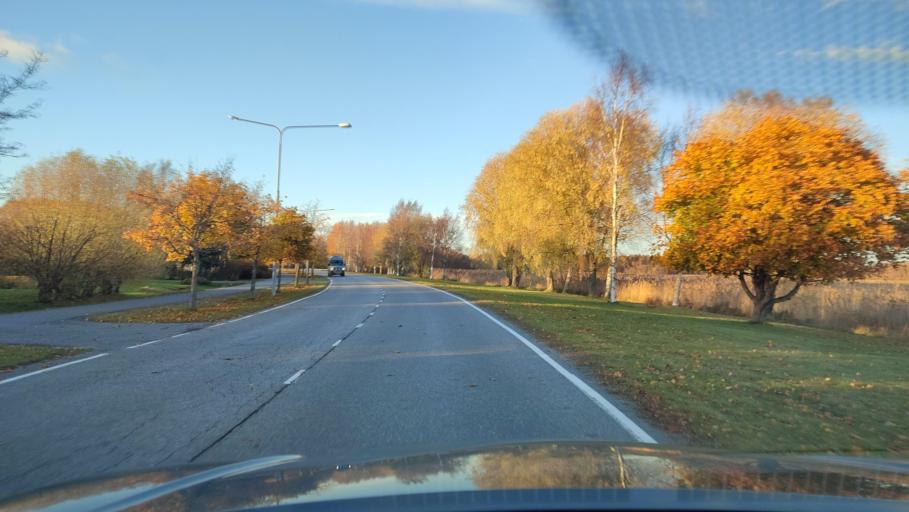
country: FI
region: Ostrobothnia
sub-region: Sydosterbotten
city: Kristinestad
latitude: 62.2792
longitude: 21.3806
